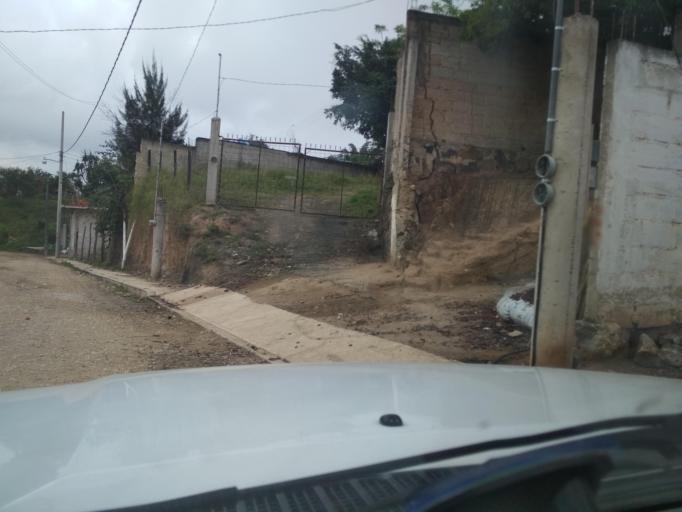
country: MX
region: Veracruz
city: El Castillo
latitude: 19.5462
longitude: -96.8297
